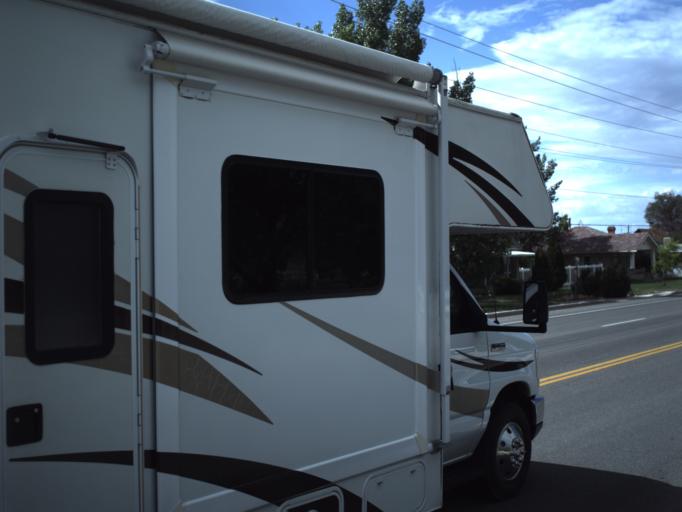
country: US
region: Utah
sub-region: Sanpete County
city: Centerfield
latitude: 39.1268
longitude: -111.8192
